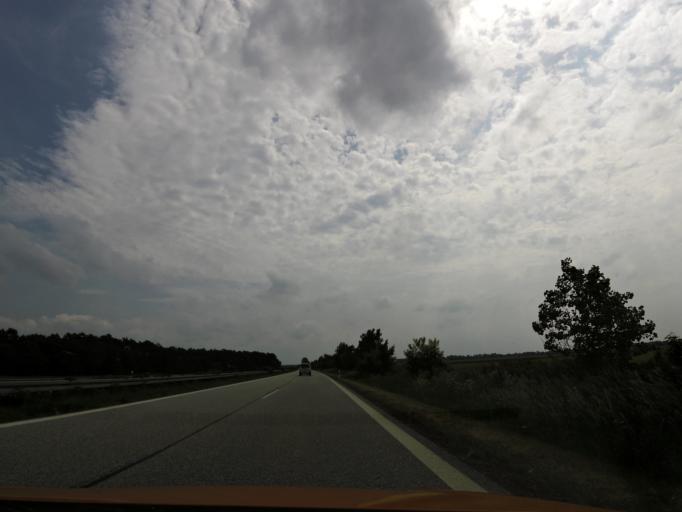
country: DE
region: Mecklenburg-Vorpommern
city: Mirow
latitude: 53.4587
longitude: 11.4956
